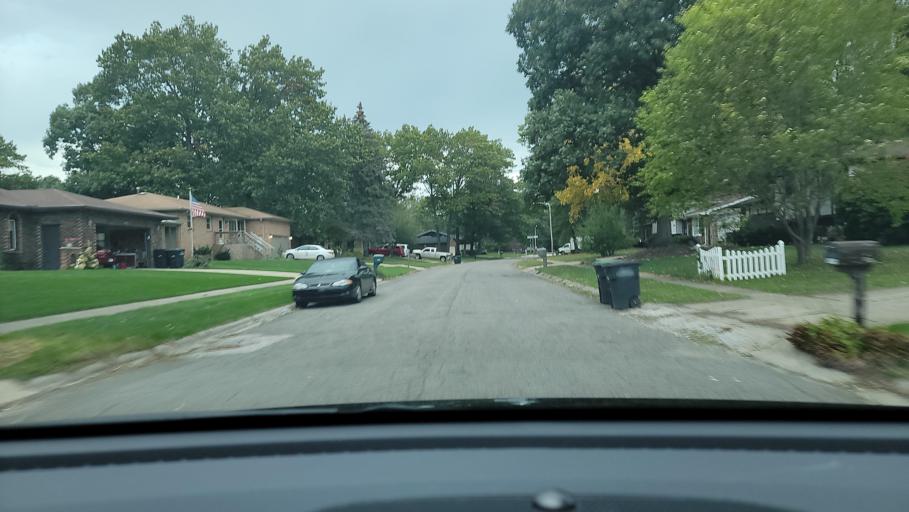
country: US
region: Indiana
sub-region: Porter County
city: Portage
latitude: 41.5696
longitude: -87.1751
